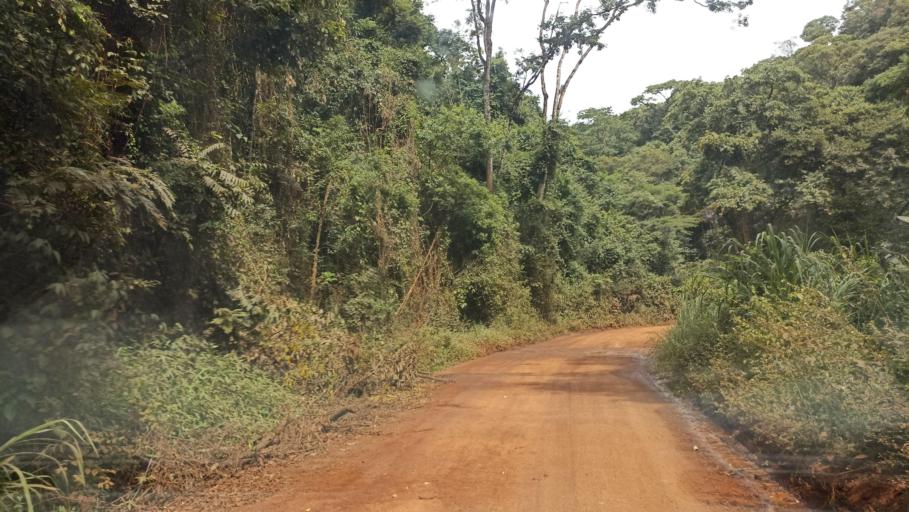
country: BR
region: Minas Gerais
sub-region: Itabirito
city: Itabirito
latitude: -20.3753
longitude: -43.7606
